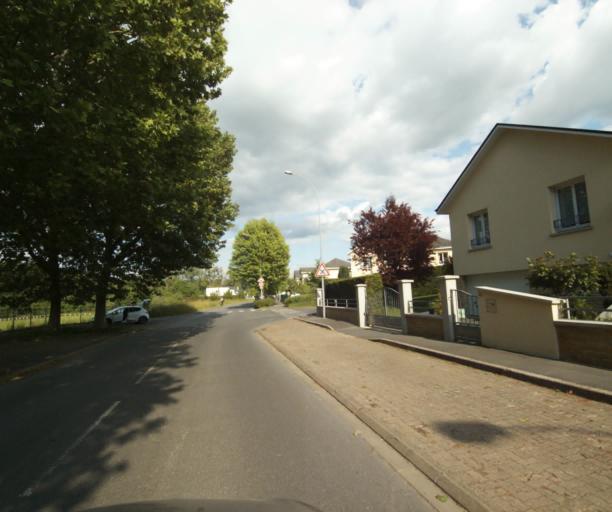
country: FR
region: Champagne-Ardenne
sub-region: Departement des Ardennes
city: Charleville-Mezieres
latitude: 49.7825
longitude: 4.7237
